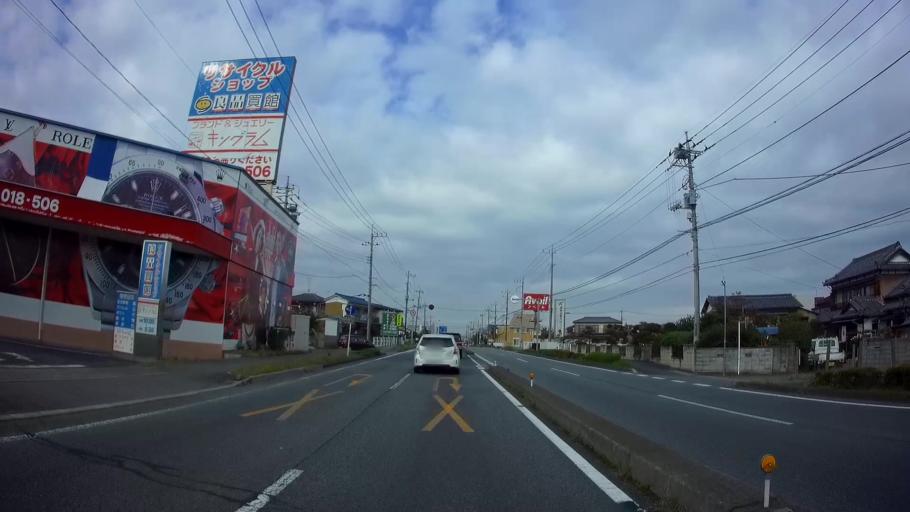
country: JP
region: Saitama
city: Konosu
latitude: 36.0688
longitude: 139.5072
